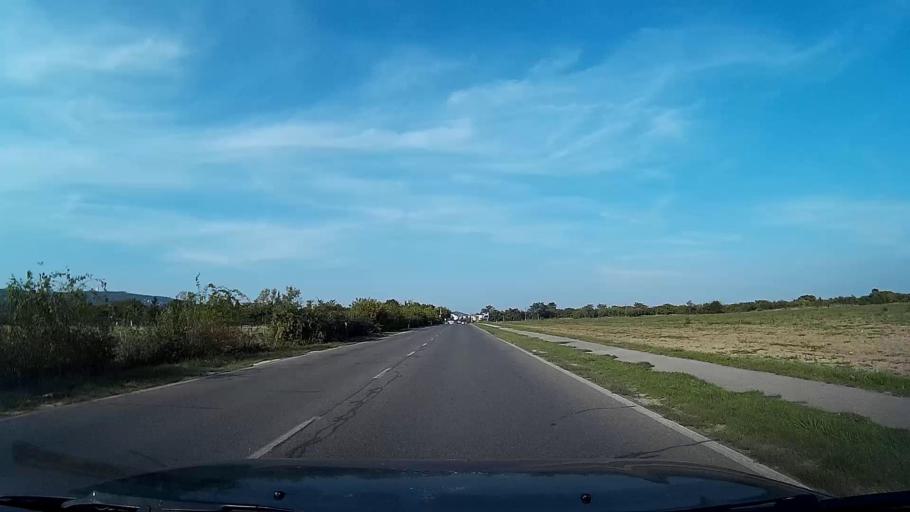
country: HU
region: Pest
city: Budaors
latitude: 47.4512
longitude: 18.9895
